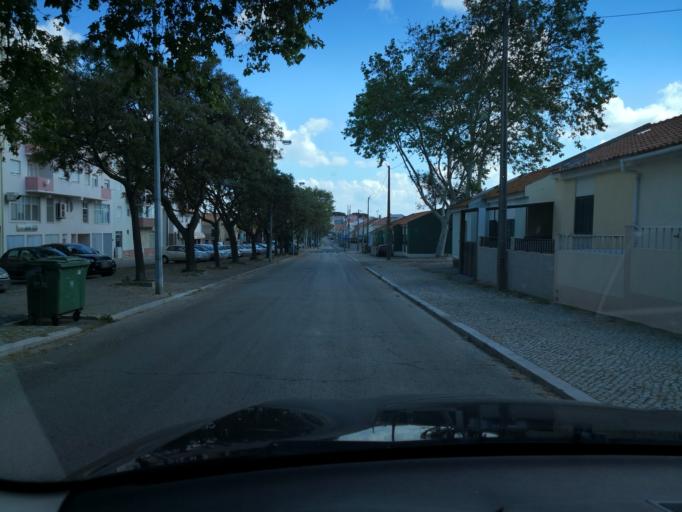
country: PT
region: Setubal
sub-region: Setubal
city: Setubal
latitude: 38.5229
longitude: -8.8642
